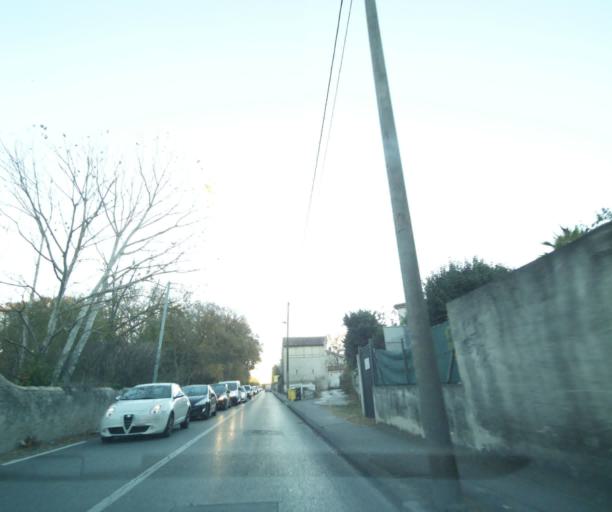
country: FR
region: Provence-Alpes-Cote d'Azur
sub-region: Departement des Bouches-du-Rhone
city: La Penne-sur-Huveaune
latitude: 43.2947
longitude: 5.4904
